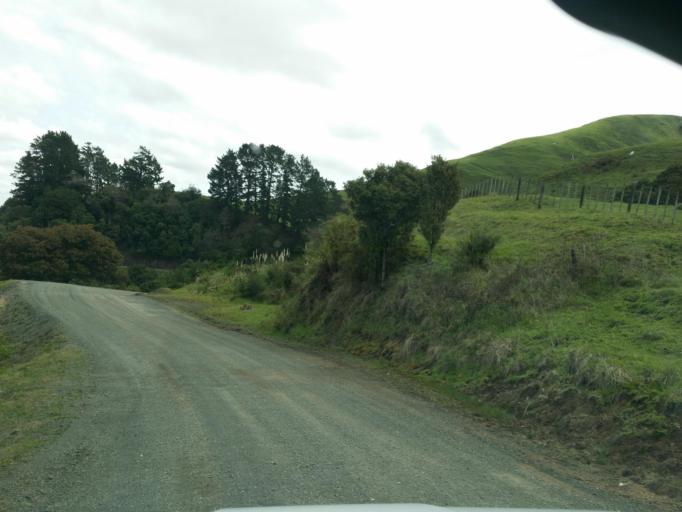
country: NZ
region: Northland
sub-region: Whangarei
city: Maungatapere
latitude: -35.9005
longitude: 174.1011
